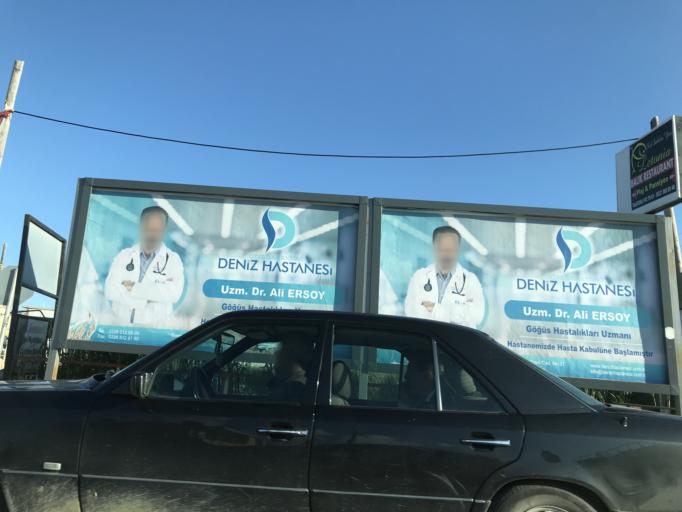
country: TR
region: Hatay
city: Samandag
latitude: 36.0815
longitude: 35.9479
